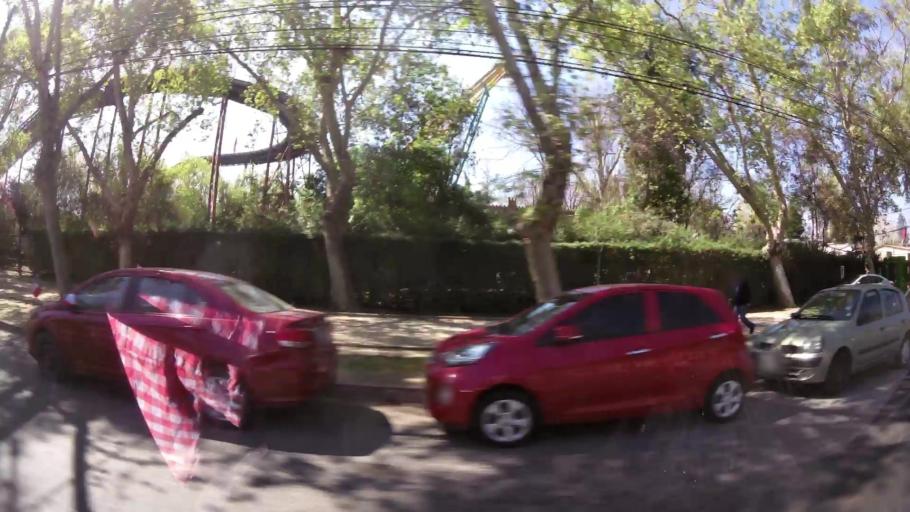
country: CL
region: Santiago Metropolitan
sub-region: Provincia de Santiago
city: Santiago
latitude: -33.4603
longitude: -70.6638
